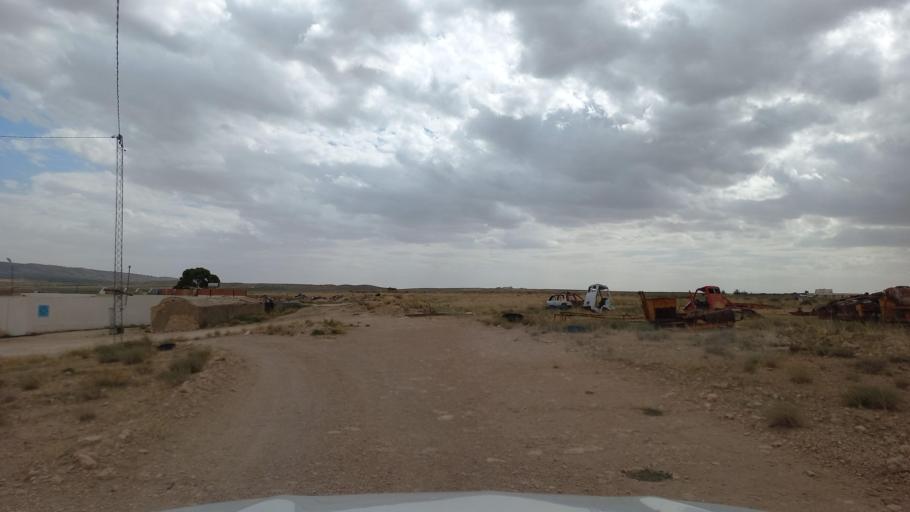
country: TN
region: Al Qasrayn
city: Sbiba
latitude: 35.3795
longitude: 9.1183
